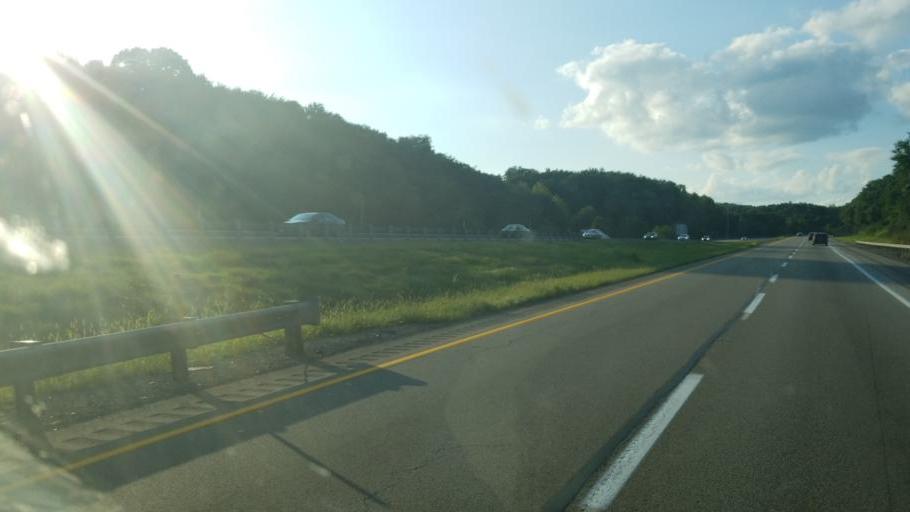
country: US
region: Pennsylvania
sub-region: Allegheny County
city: Franklin Park
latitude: 40.5677
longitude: -80.1150
